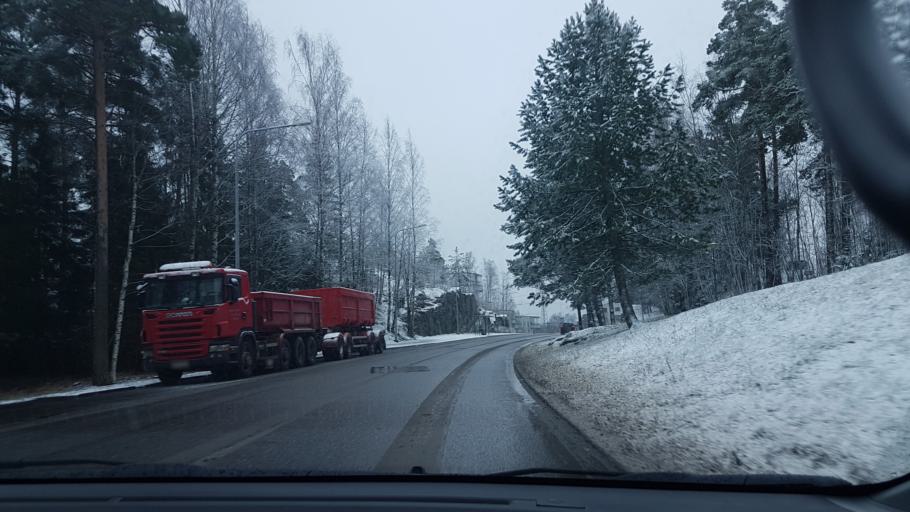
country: FI
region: Uusimaa
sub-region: Helsinki
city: Vantaa
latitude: 60.2342
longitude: 25.1288
